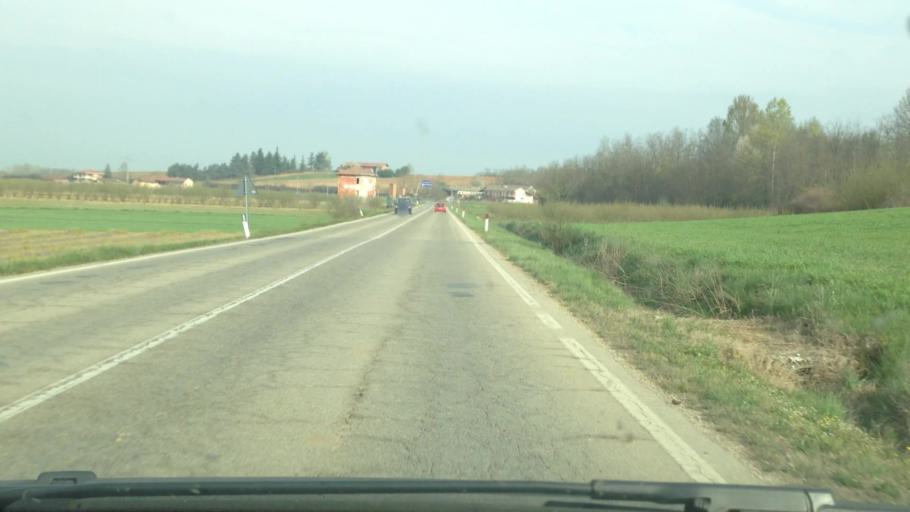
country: IT
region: Piedmont
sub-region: Provincia di Cuneo
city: Monta
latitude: 44.8317
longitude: 7.9261
